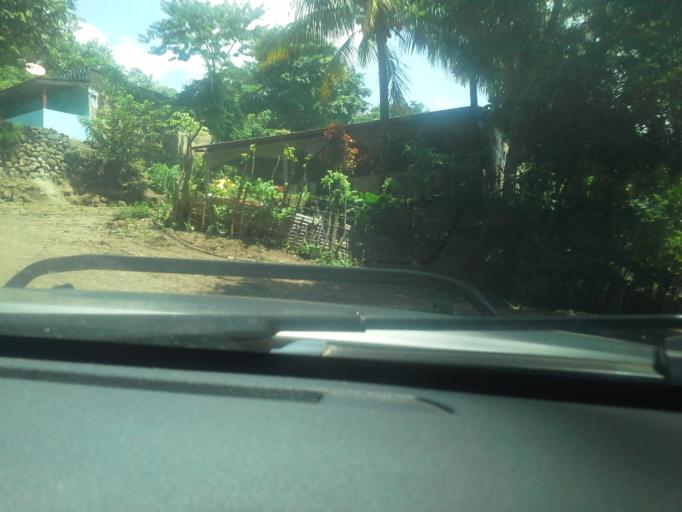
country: NI
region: Matagalpa
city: Terrabona
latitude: 12.7534
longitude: -85.9266
